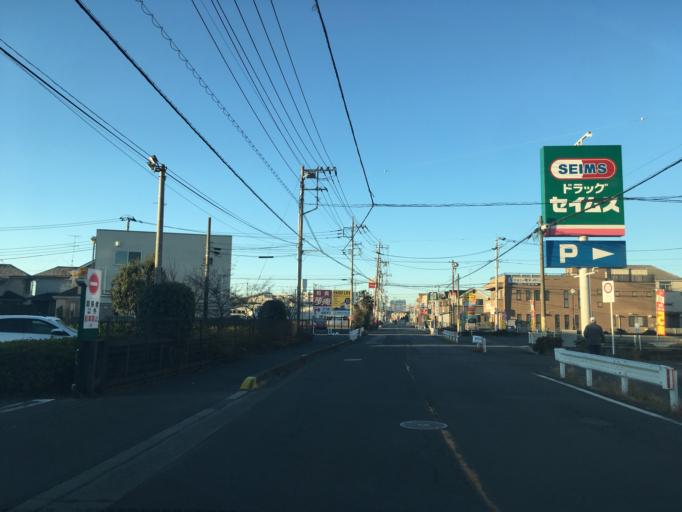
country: JP
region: Saitama
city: Sayama
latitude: 35.8257
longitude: 139.4032
